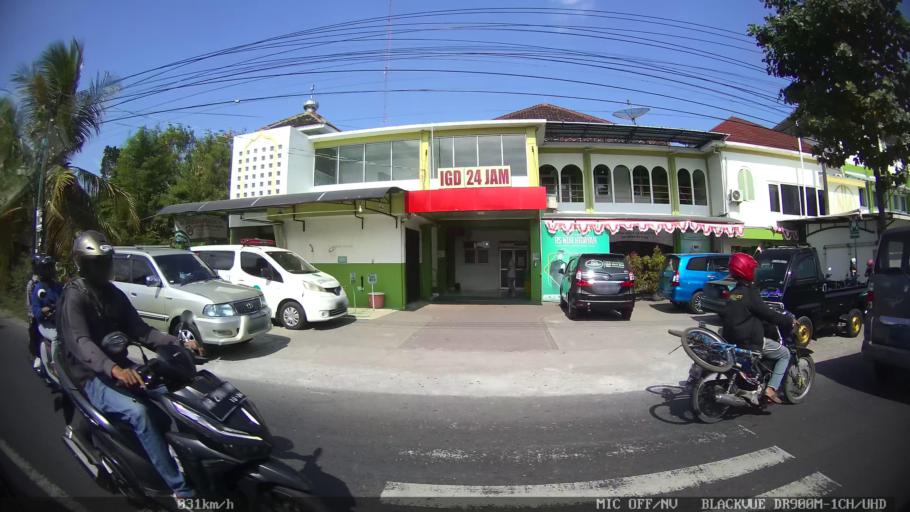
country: ID
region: Daerah Istimewa Yogyakarta
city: Sewon
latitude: -7.8862
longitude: 110.3880
